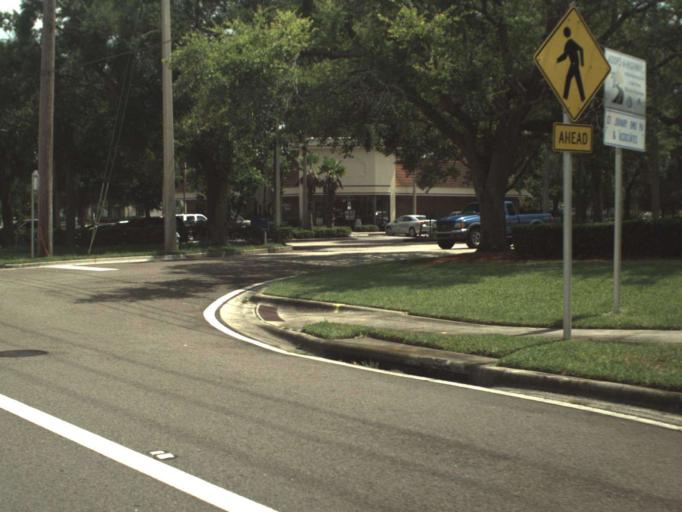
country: US
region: Florida
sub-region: Seminole County
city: Forest City
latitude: 28.6641
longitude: -81.4189
